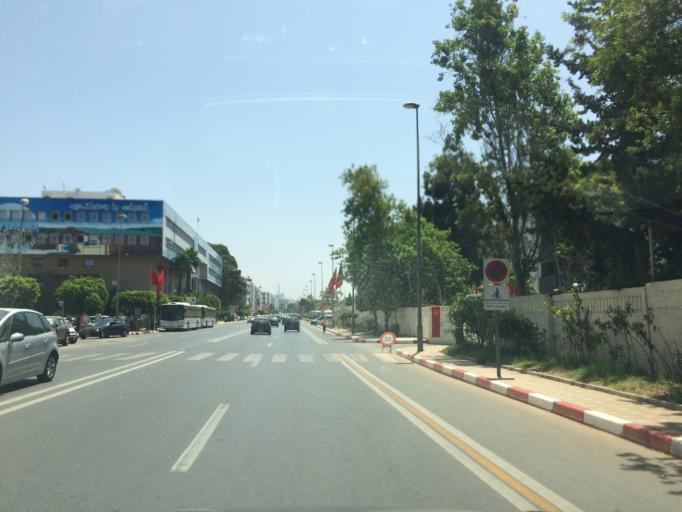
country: MA
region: Rabat-Sale-Zemmour-Zaer
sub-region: Rabat
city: Rabat
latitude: 33.9938
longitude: -6.8514
